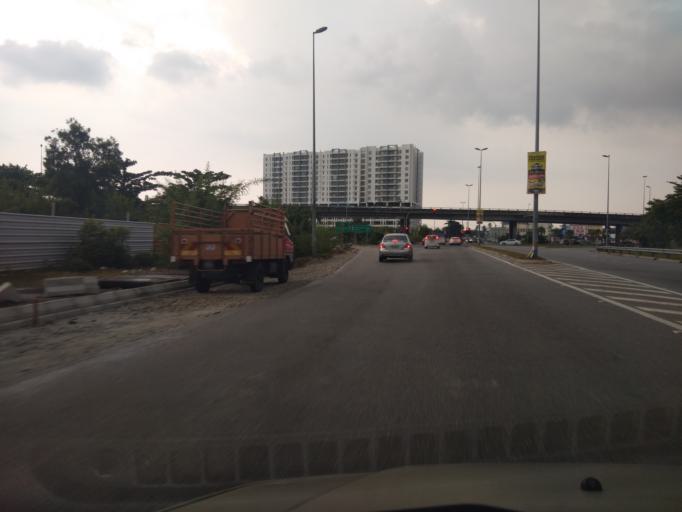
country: MY
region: Penang
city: Permatang Kuching
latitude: 5.4414
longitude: 100.3815
